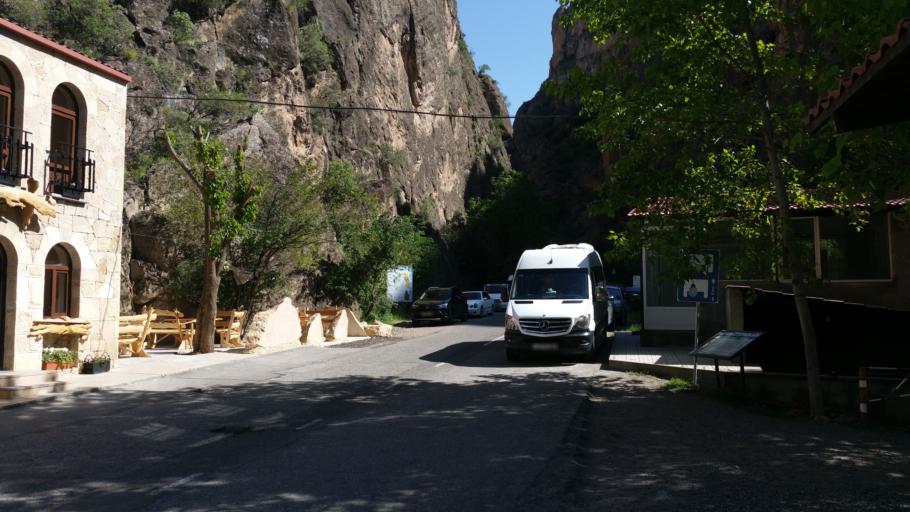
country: AM
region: Vayots' Dzori Marz
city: Areni
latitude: 39.7317
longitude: 45.2043
